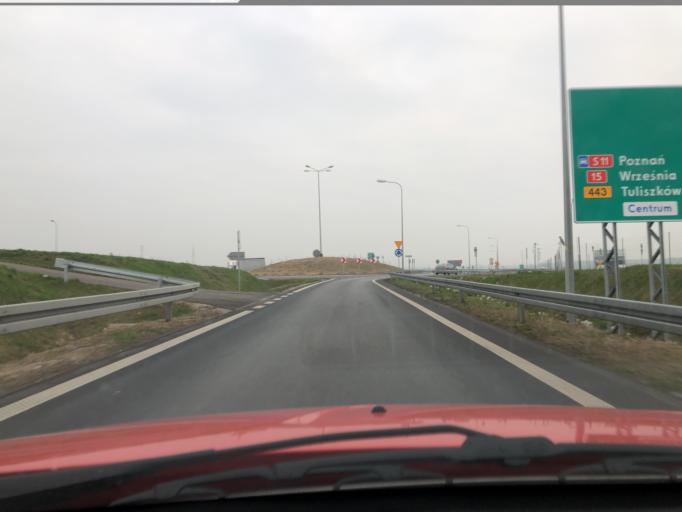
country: PL
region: Greater Poland Voivodeship
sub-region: Powiat jarocinski
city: Jarocin
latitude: 51.9776
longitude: 17.5224
